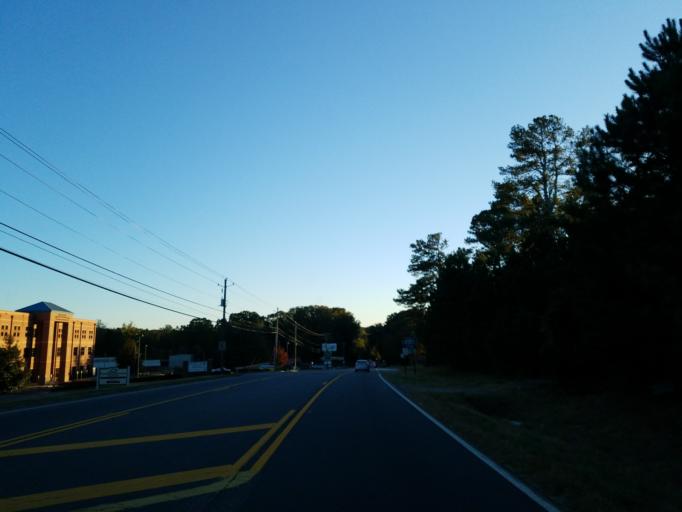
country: US
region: Georgia
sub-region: Forsyth County
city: Cumming
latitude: 34.2336
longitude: -84.1238
